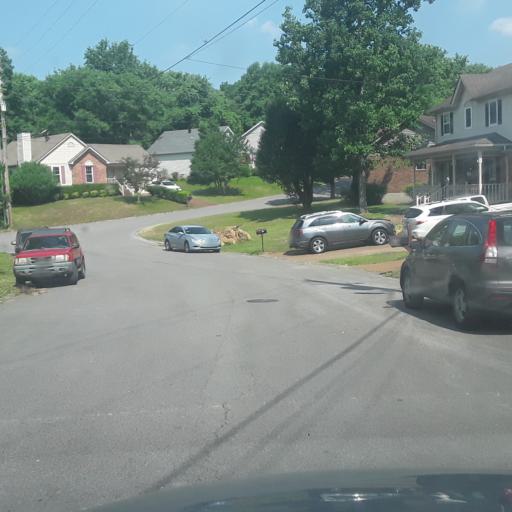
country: US
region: Tennessee
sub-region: Williamson County
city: Brentwood Estates
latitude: 36.0300
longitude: -86.7084
